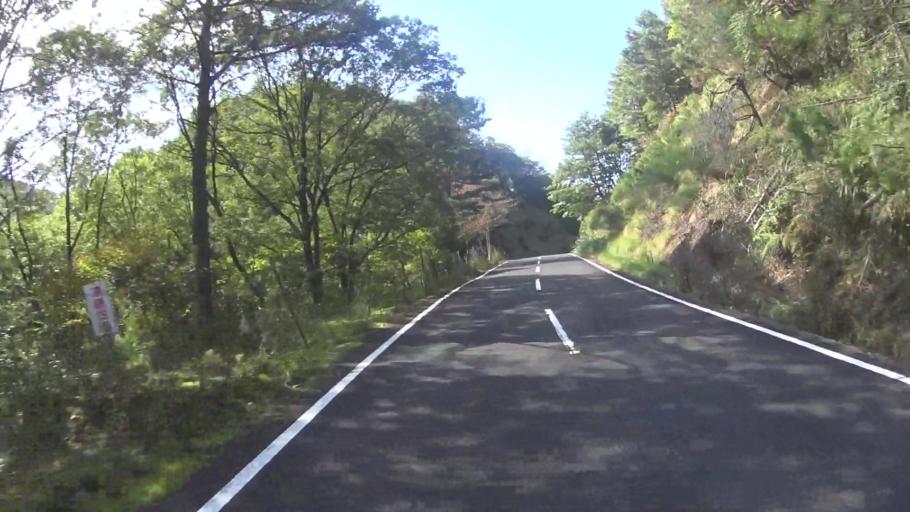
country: JP
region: Hyogo
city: Toyooka
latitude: 35.5365
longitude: 134.9198
